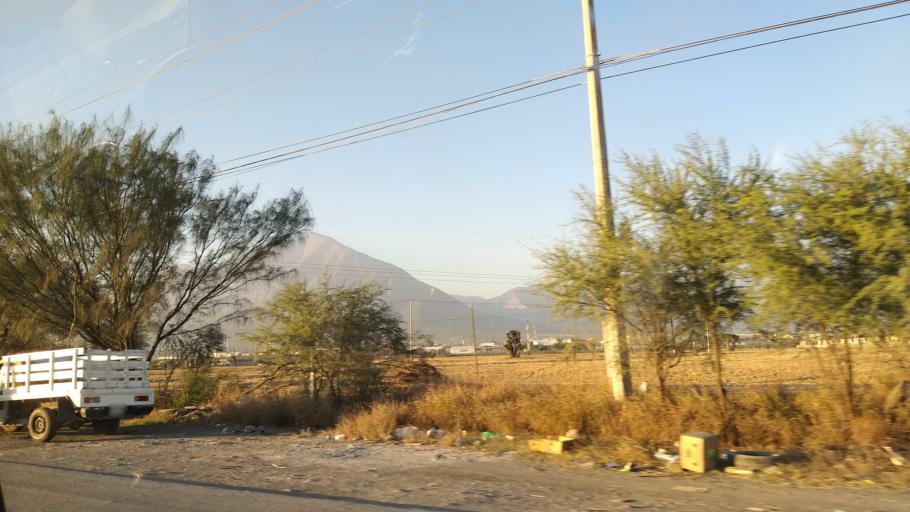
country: MX
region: Nuevo Leon
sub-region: Garcia
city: Parque Industrial Ciudad Mitras
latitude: 25.7772
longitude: -100.4409
